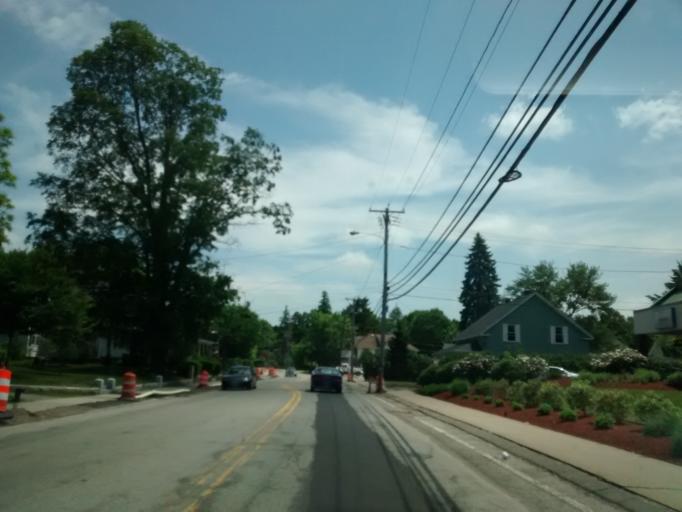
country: US
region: Massachusetts
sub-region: Worcester County
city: Uxbridge
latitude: 42.0822
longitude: -71.6378
